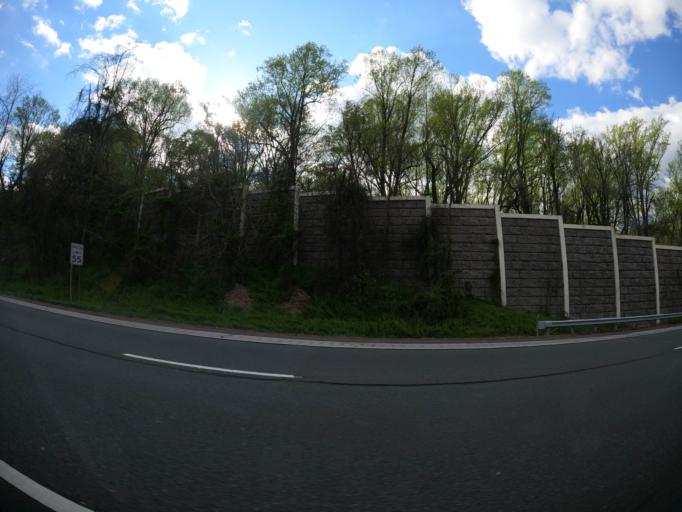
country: US
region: Maryland
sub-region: Howard County
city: Ellicott City
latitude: 39.2656
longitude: -76.8122
